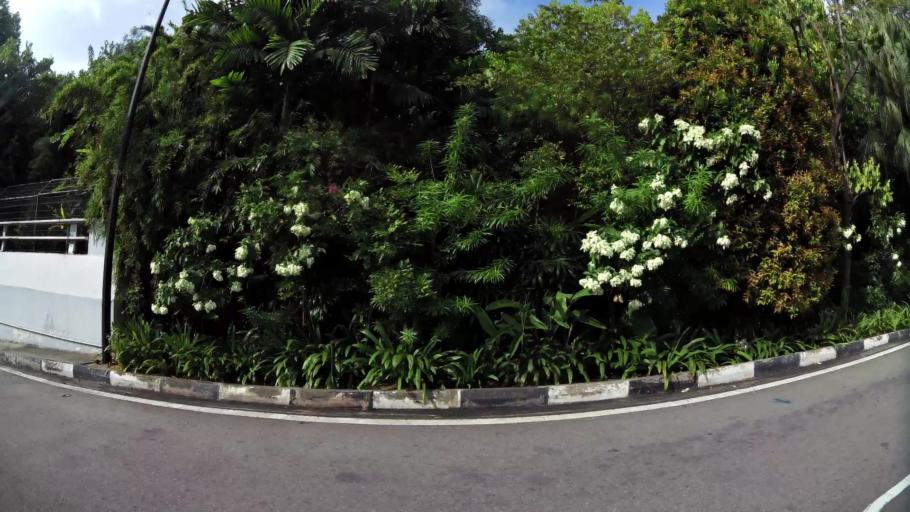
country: SG
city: Singapore
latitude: 1.2559
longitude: 103.8239
